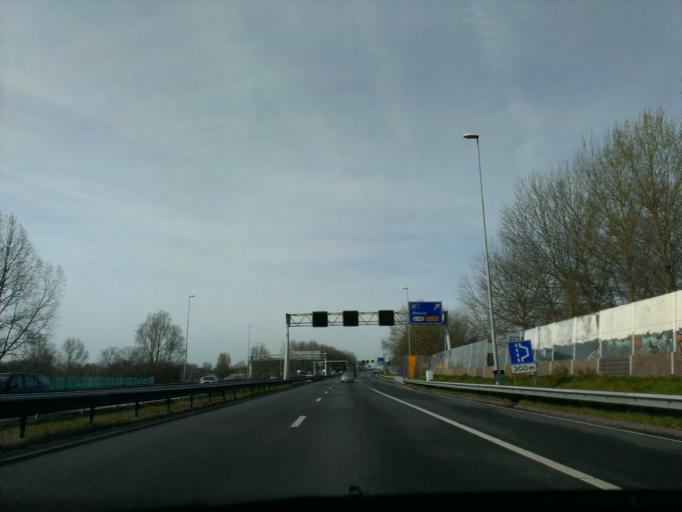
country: NL
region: North Holland
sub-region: Gemeente Amsterdam
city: Amsterdam-Zuidoost
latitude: 52.3155
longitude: 4.9924
